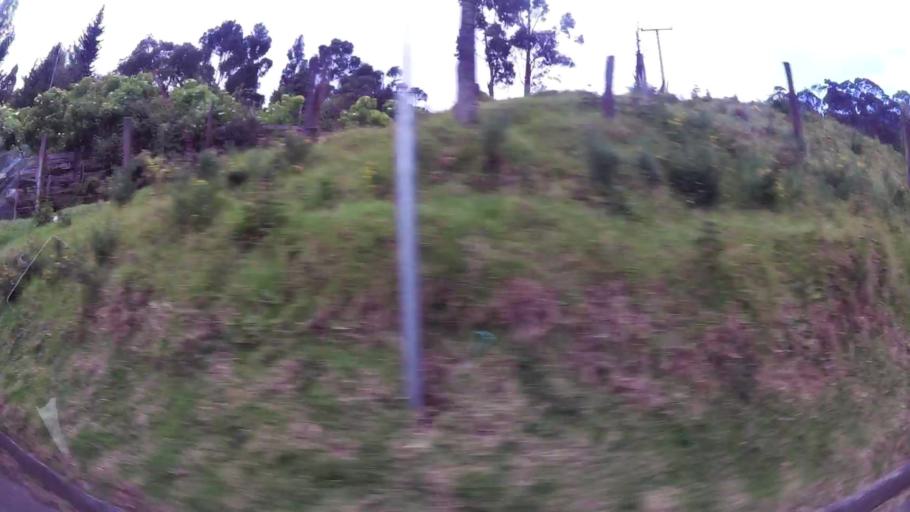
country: CO
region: Bogota D.C.
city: Bogota
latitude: 4.5957
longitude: -74.0657
